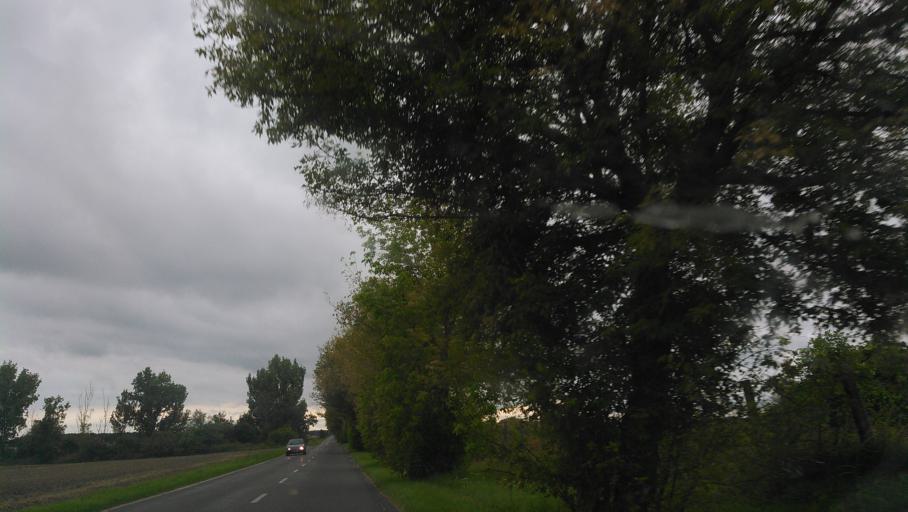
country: SK
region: Trnavsky
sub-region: Okres Dunajska Streda
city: Velky Meder
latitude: 47.9224
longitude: 17.7402
